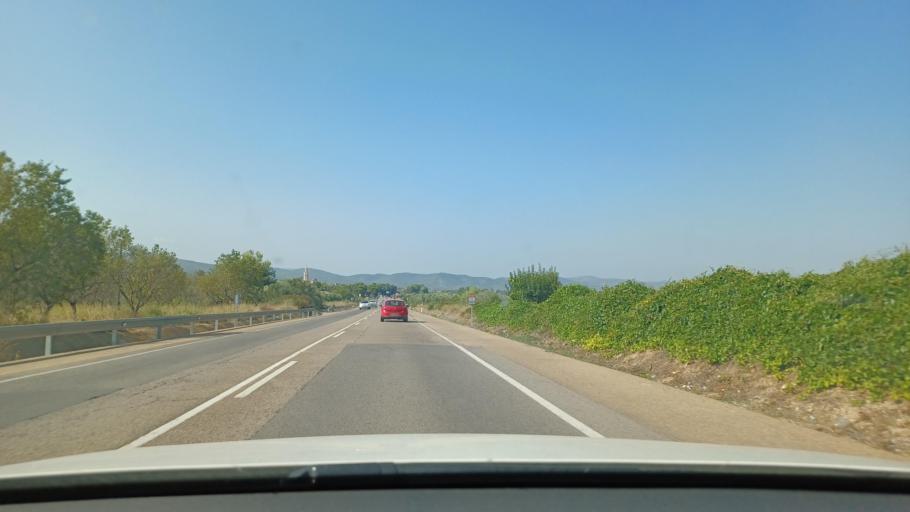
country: ES
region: Valencia
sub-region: Provincia de Castello
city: Alcala de Xivert
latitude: 40.2892
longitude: 0.2254
